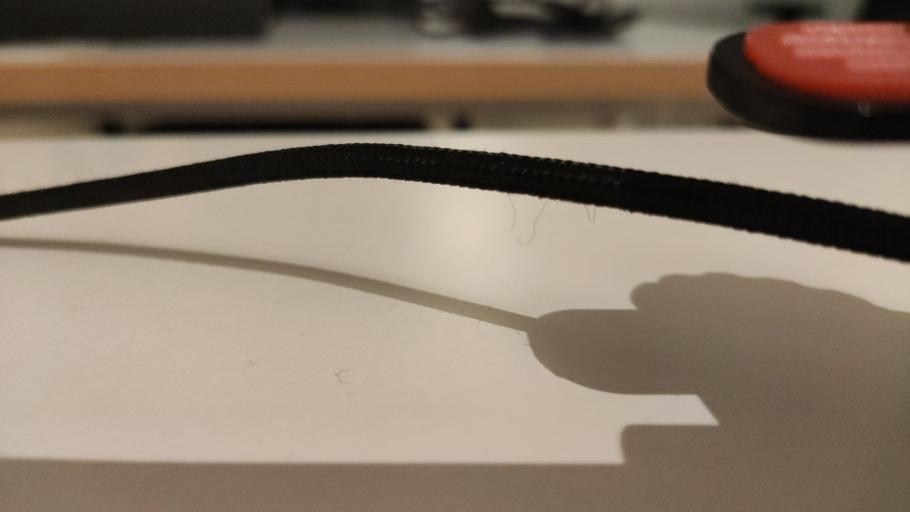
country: RU
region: Moskovskaya
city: Orekhovo-Zuyevo
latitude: 55.8429
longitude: 38.9659
